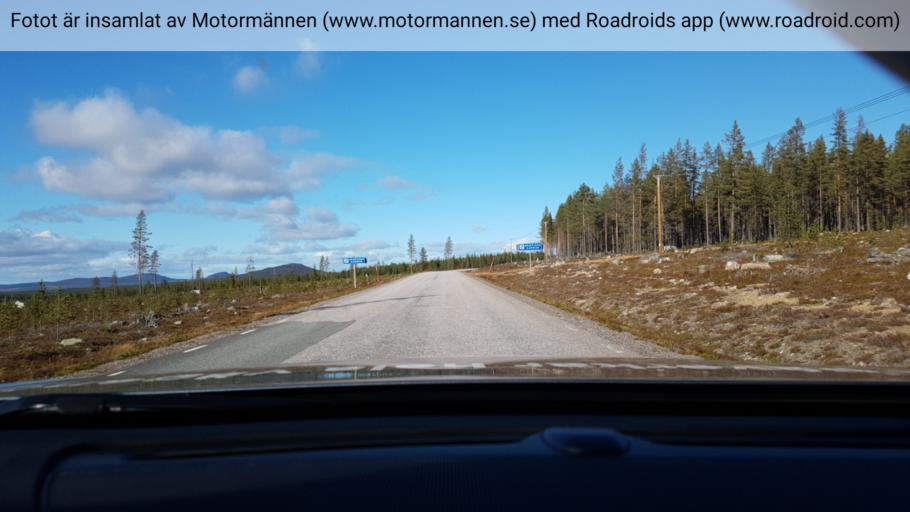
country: SE
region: Vaesterbotten
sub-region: Mala Kommun
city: Mala
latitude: 65.7760
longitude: 18.5176
